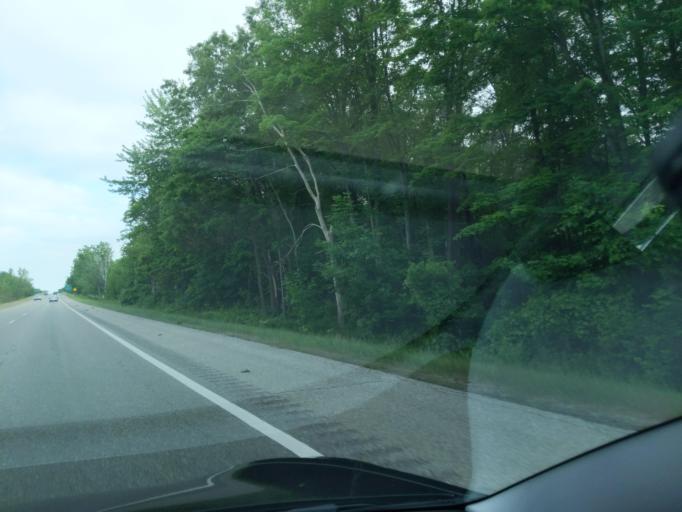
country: US
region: Michigan
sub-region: Muskegon County
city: Lakewood Club
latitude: 43.3438
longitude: -86.2460
